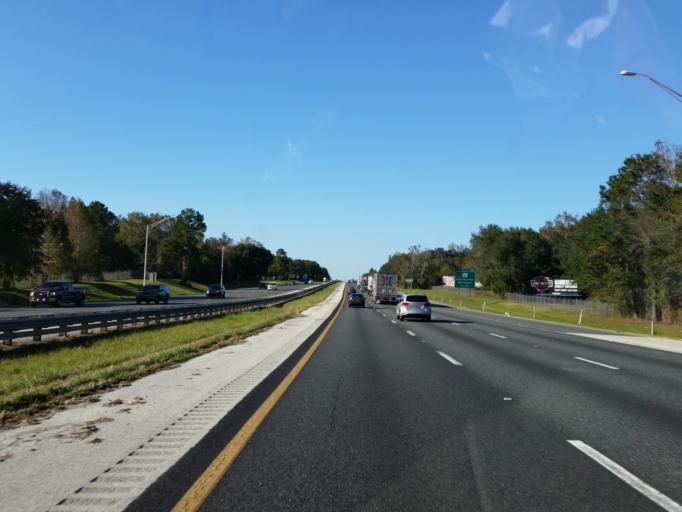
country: US
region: Florida
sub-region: Alachua County
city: Gainesville
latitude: 29.5920
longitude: -82.3641
